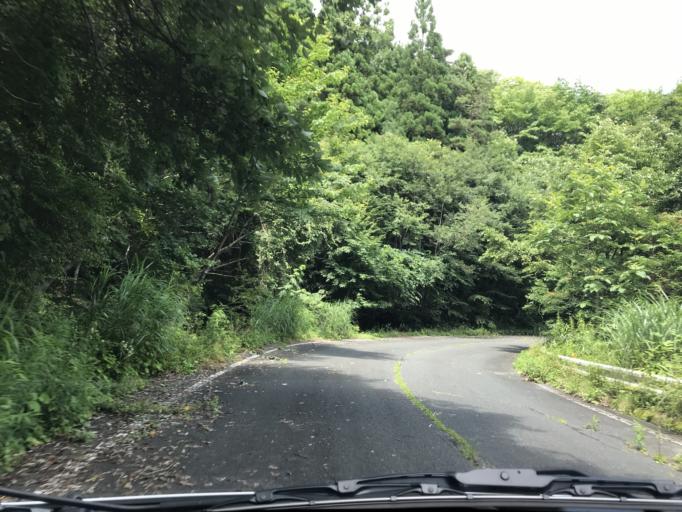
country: JP
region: Iwate
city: Tono
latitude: 39.0924
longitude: 141.4141
